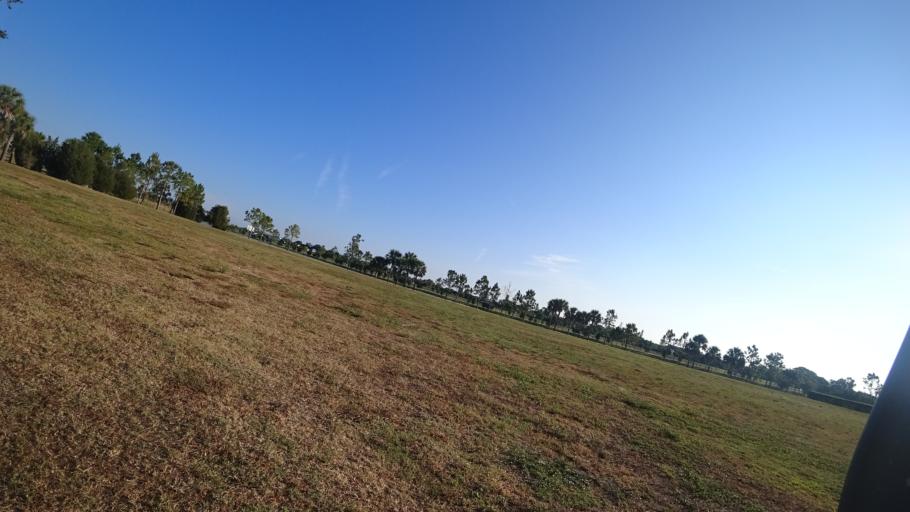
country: US
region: Florida
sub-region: Manatee County
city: Ellenton
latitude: 27.5015
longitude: -82.4855
